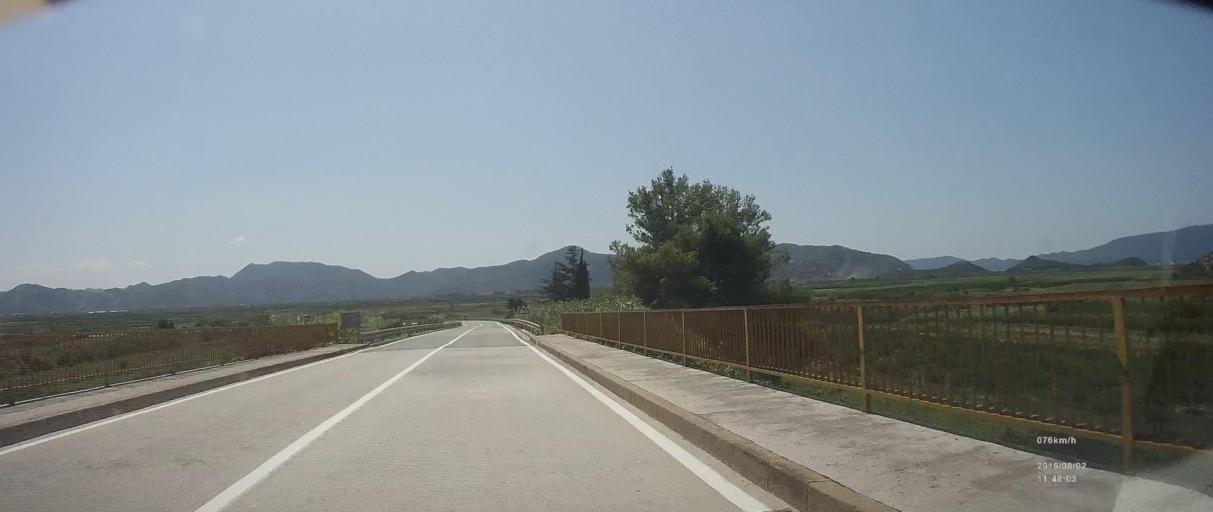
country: HR
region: Dubrovacko-Neretvanska
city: Komin
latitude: 43.0371
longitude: 17.4856
